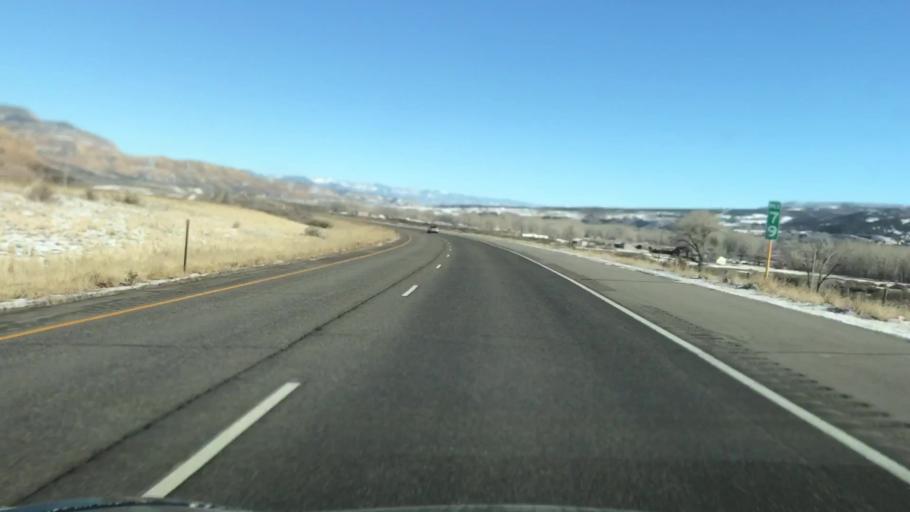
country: US
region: Colorado
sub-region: Garfield County
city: Battlement Mesa
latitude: 39.4783
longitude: -107.9751
